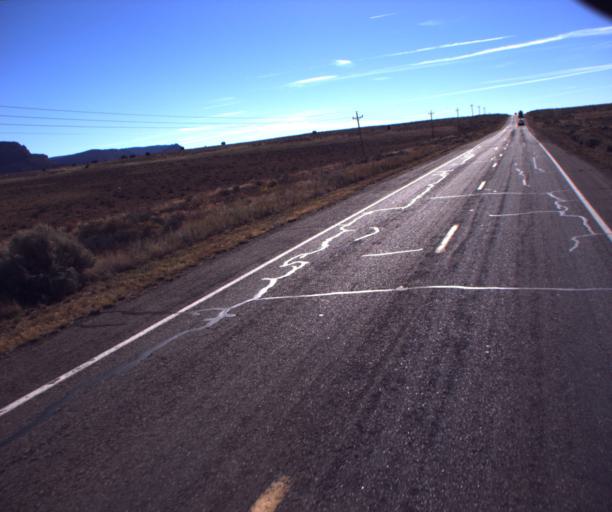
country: US
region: Arizona
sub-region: Mohave County
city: Colorado City
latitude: 36.9200
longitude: -112.9349
